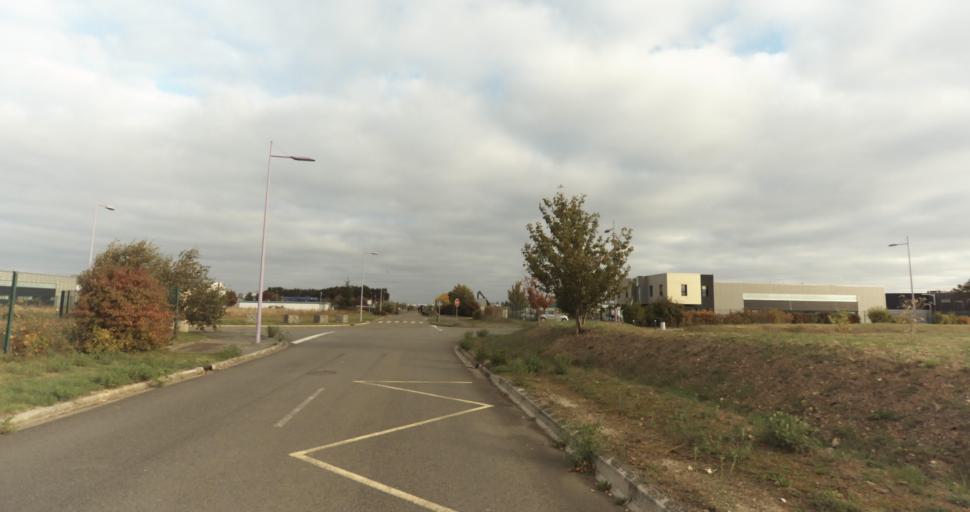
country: FR
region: Centre
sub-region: Departement d'Eure-et-Loir
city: Vernouillet
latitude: 48.7114
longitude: 1.3758
